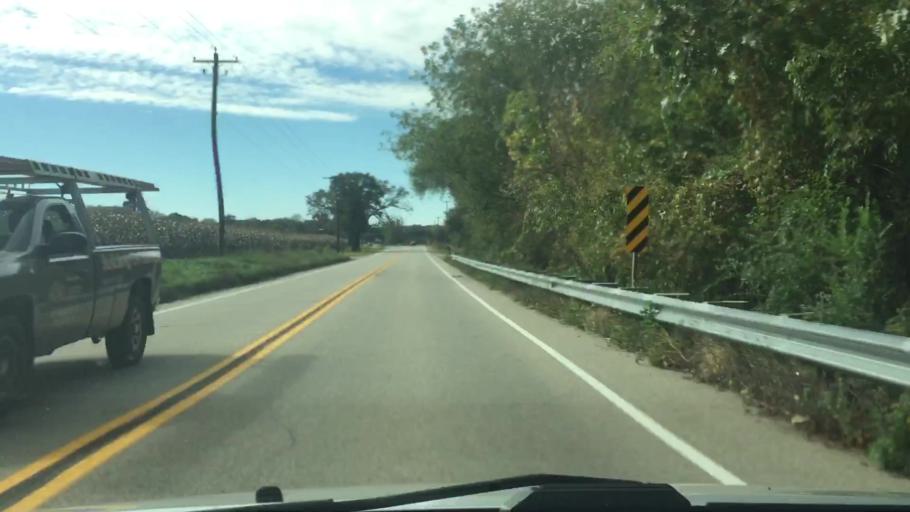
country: US
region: Wisconsin
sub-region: Waukesha County
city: Dousman
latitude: 42.9624
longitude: -88.4765
